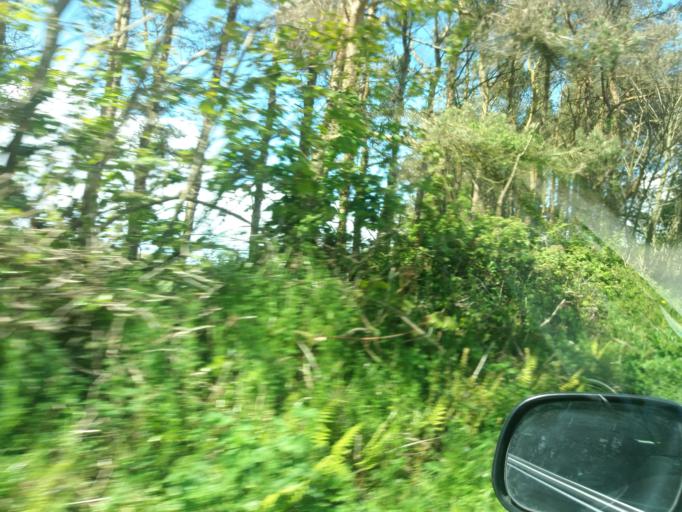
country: IE
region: Munster
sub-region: Waterford
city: Dunmore East
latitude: 52.2343
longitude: -6.9323
